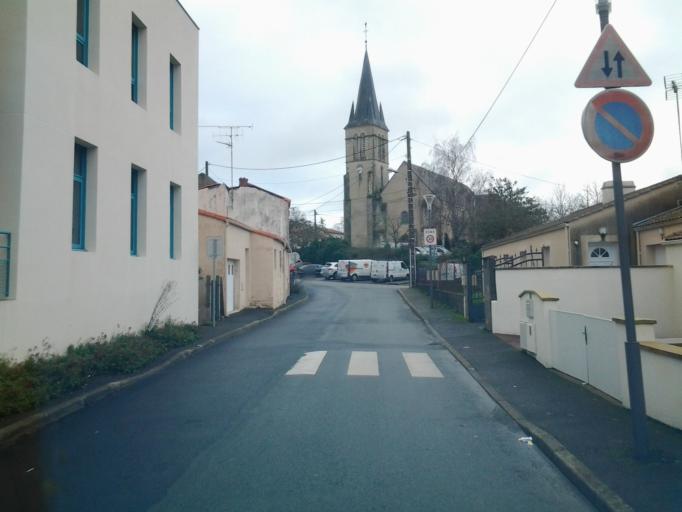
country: FR
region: Pays de la Loire
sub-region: Departement de la Vendee
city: La Roche-sur-Yon
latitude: 46.6604
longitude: -1.4032
